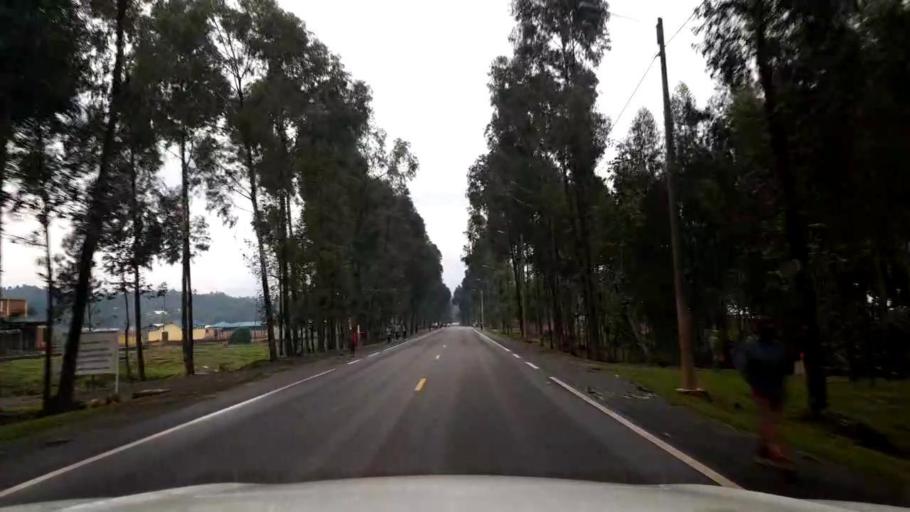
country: RW
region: Northern Province
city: Musanze
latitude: -1.5283
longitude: 29.5730
